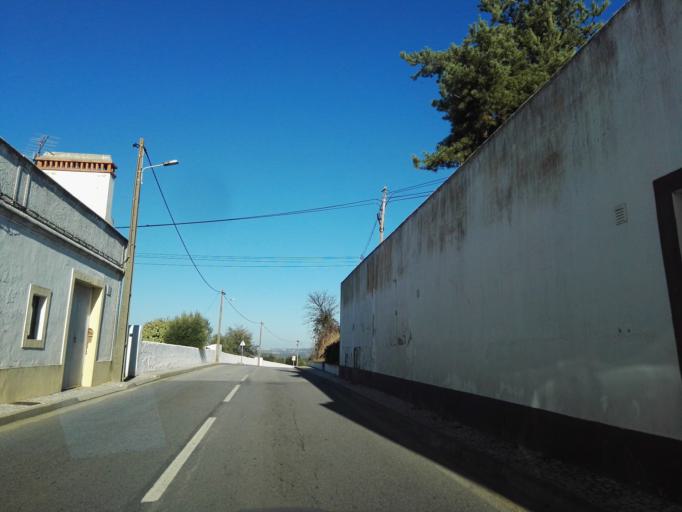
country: PT
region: Evora
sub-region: Estremoz
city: Estremoz
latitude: 38.7654
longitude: -7.7157
